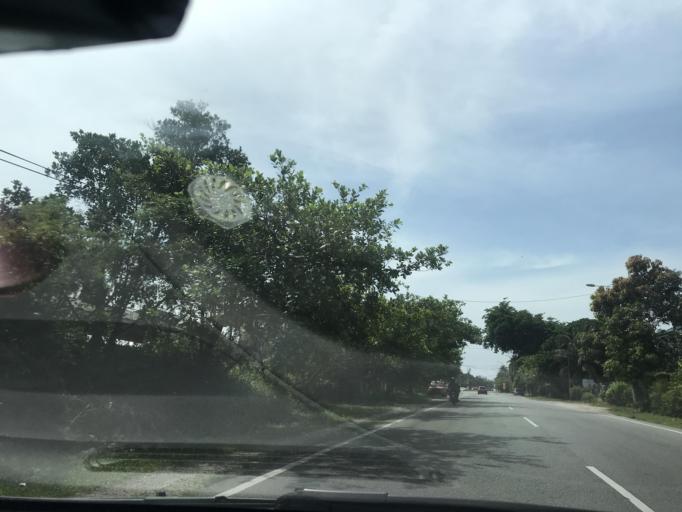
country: MY
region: Kelantan
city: Tumpat
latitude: 6.1855
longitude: 102.1654
